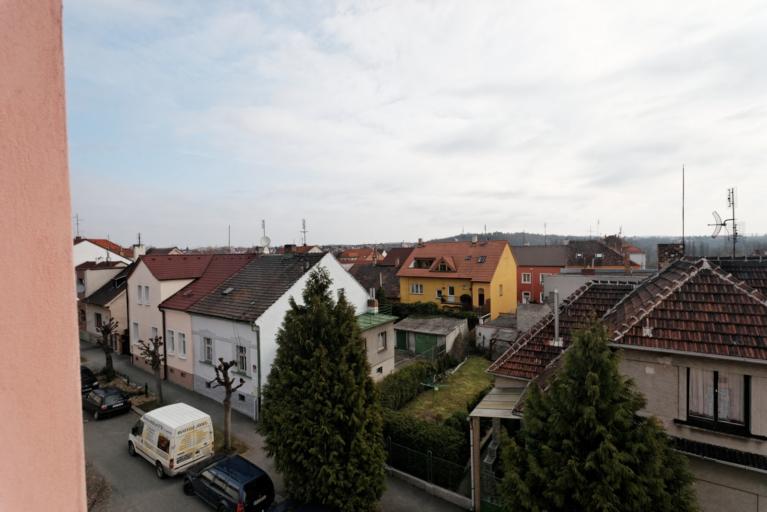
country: CZ
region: Plzensky
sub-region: Okres Plzen-Mesto
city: Pilsen
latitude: 49.7212
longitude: 13.3840
